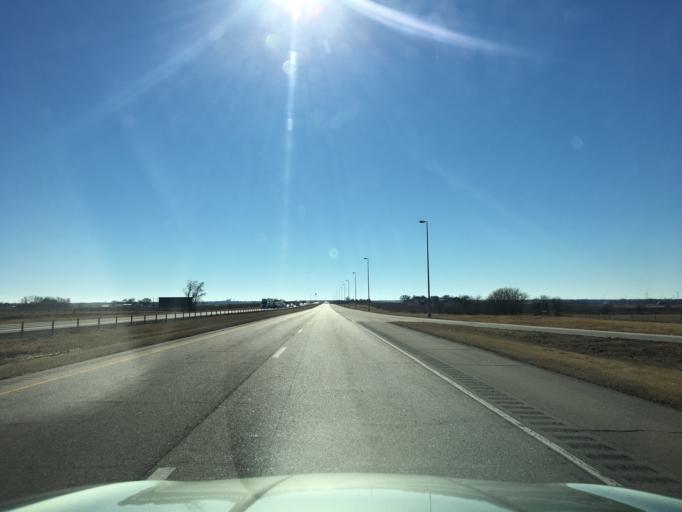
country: US
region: Oklahoma
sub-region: Kay County
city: Blackwell
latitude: 36.9801
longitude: -97.3458
